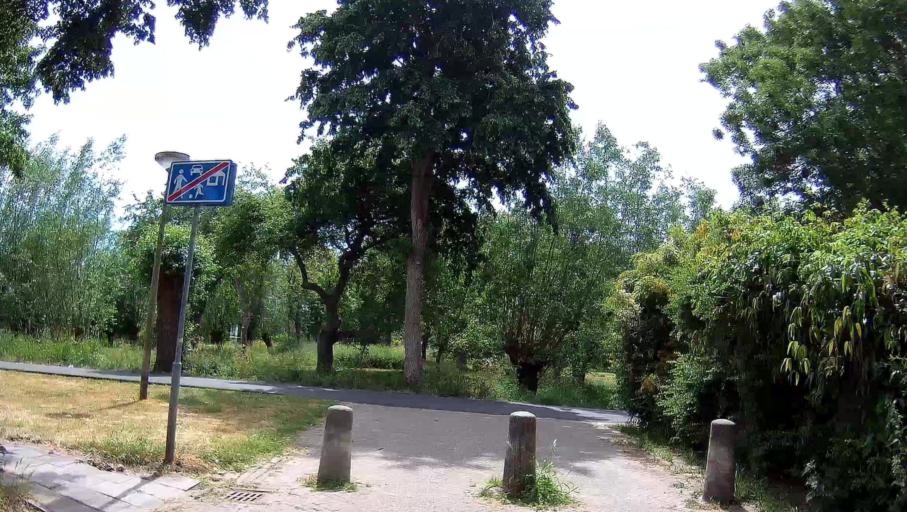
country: NL
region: South Holland
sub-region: Gemeente Delft
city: Delft
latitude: 51.9837
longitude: 4.3511
